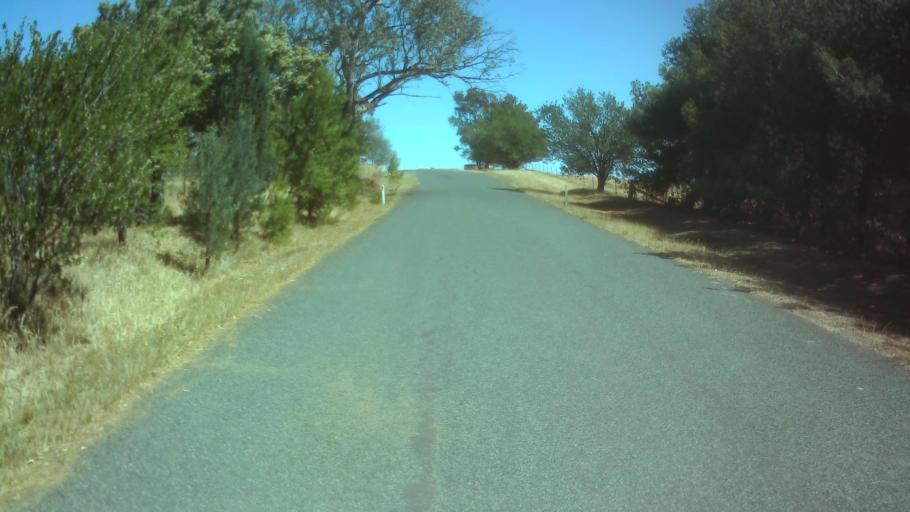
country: AU
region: New South Wales
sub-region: Weddin
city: Grenfell
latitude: -33.9476
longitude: 148.3933
